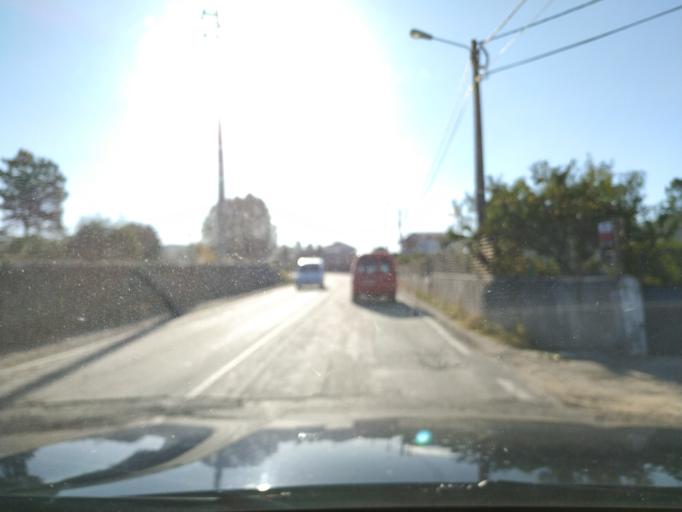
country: PT
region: Aveiro
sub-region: Vale de Cambra
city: Vale de Cambra
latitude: 40.8797
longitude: -8.4220
